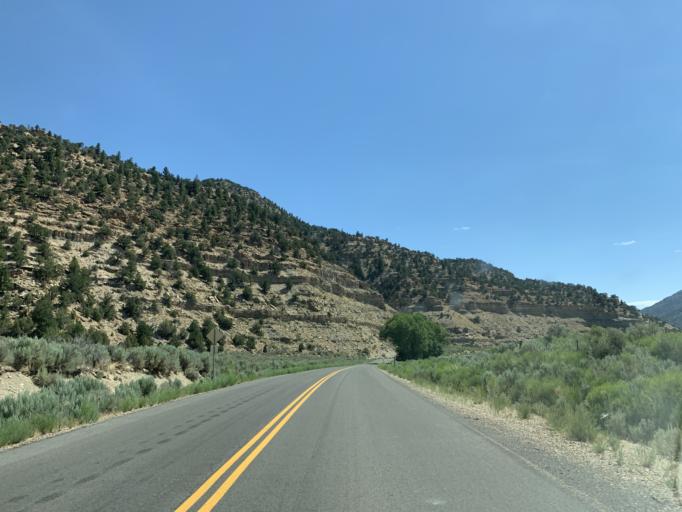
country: US
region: Utah
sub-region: Carbon County
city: East Carbon City
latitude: 39.7780
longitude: -110.4523
